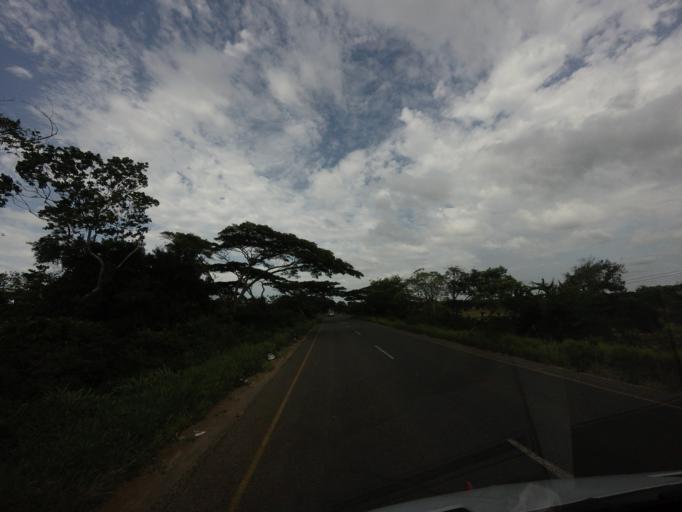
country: ZA
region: KwaZulu-Natal
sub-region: uMkhanyakude District Municipality
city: Mtubatuba
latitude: -28.3829
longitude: 32.3554
